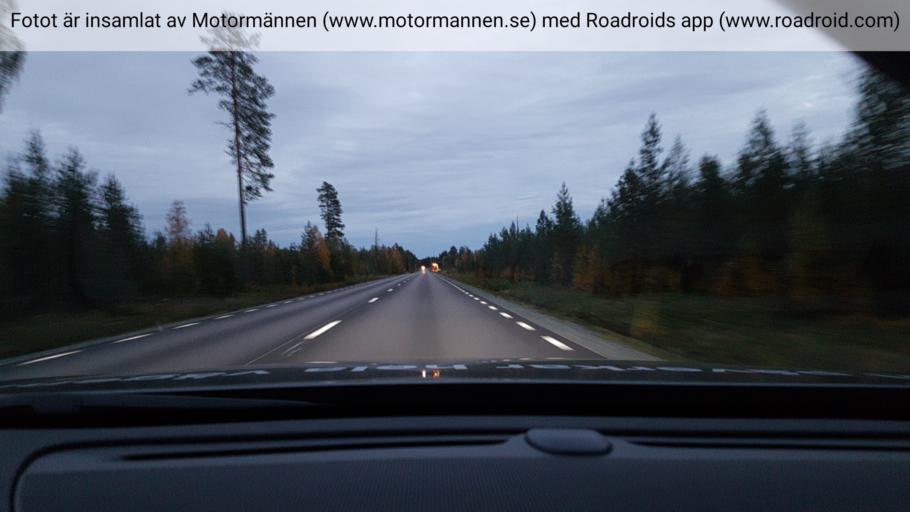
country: SE
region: Norrbotten
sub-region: Alvsbyns Kommun
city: AElvsbyn
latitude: 65.7538
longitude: 20.8993
